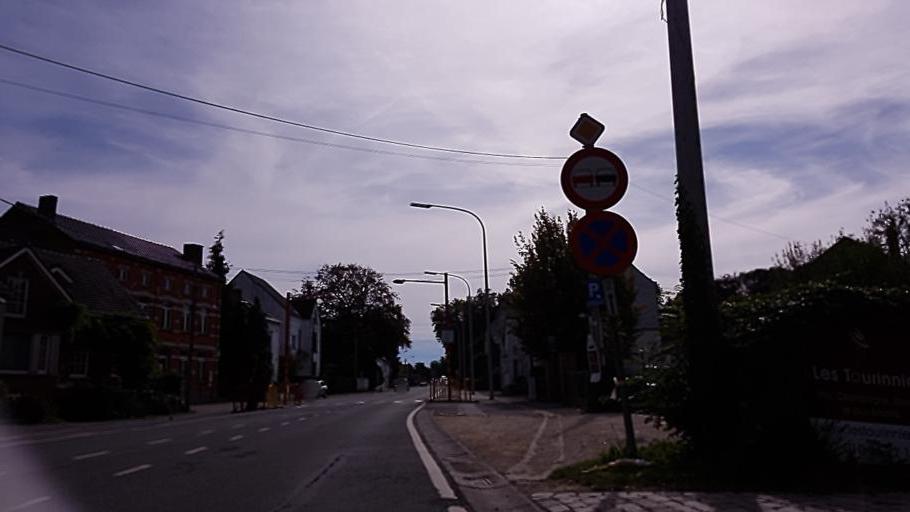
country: BE
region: Wallonia
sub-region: Province du Brabant Wallon
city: Grez-Doiceau
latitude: 50.7789
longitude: 4.7174
